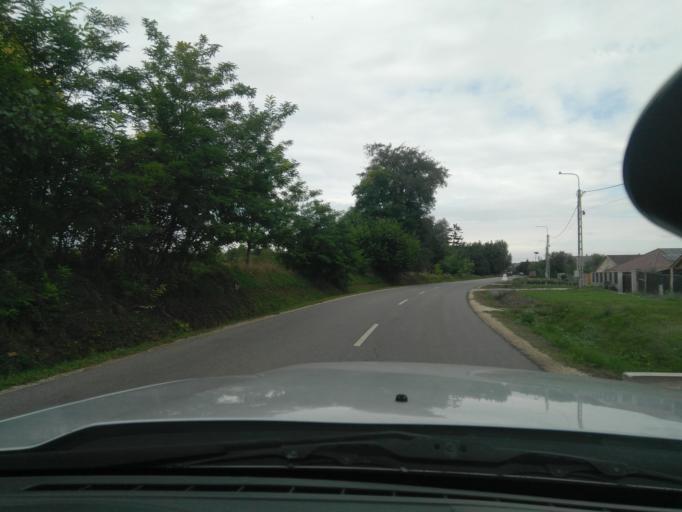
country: HU
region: Fejer
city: Val
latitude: 47.3587
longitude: 18.7358
